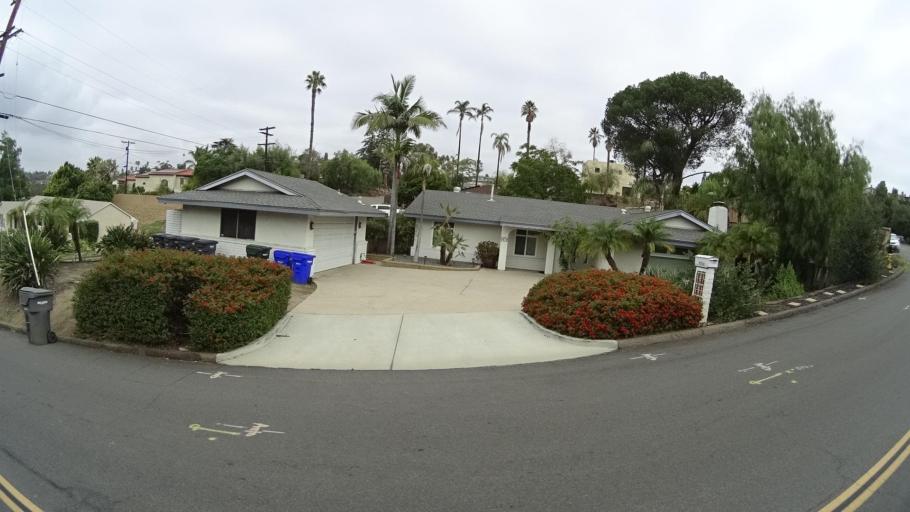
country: US
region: California
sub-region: San Diego County
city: Spring Valley
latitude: 32.7579
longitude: -116.9929
